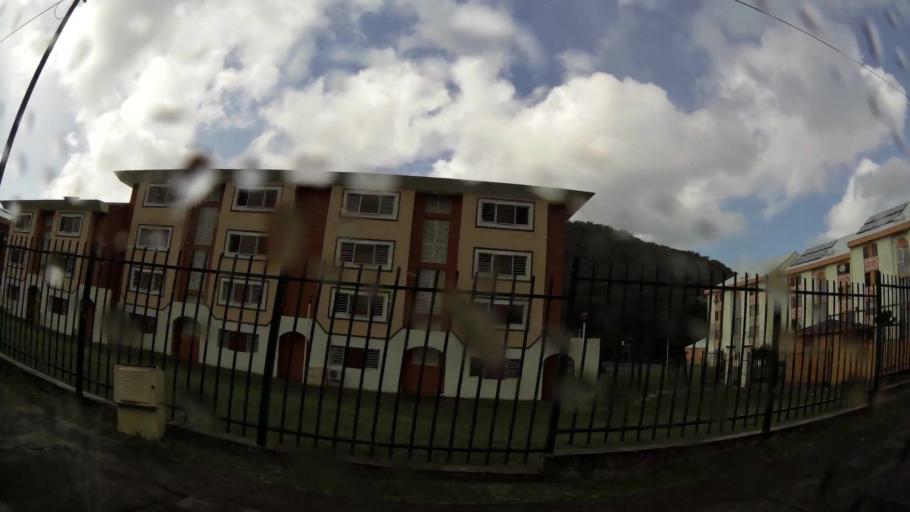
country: MQ
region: Martinique
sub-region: Martinique
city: Les Trois-Ilets
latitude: 14.4972
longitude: -61.0787
